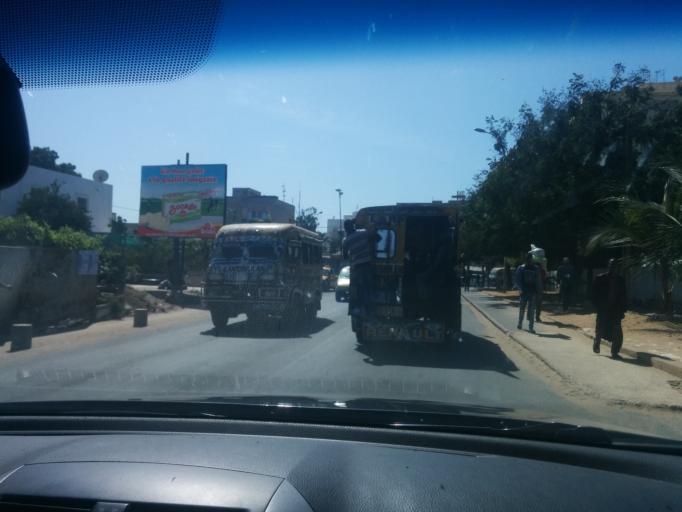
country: SN
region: Dakar
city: Grand Dakar
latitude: 14.7277
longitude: -17.4466
